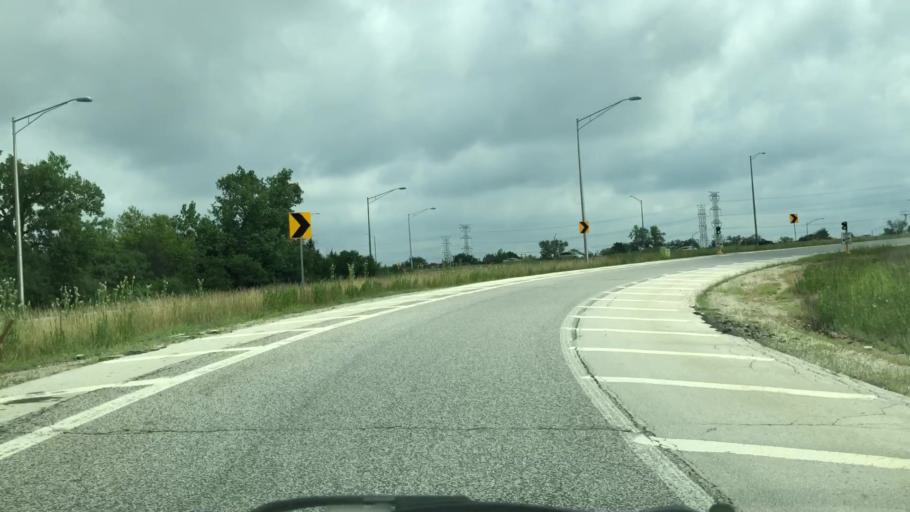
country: US
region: Illinois
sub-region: DuPage County
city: Addison
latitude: 41.9288
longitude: -87.9647
